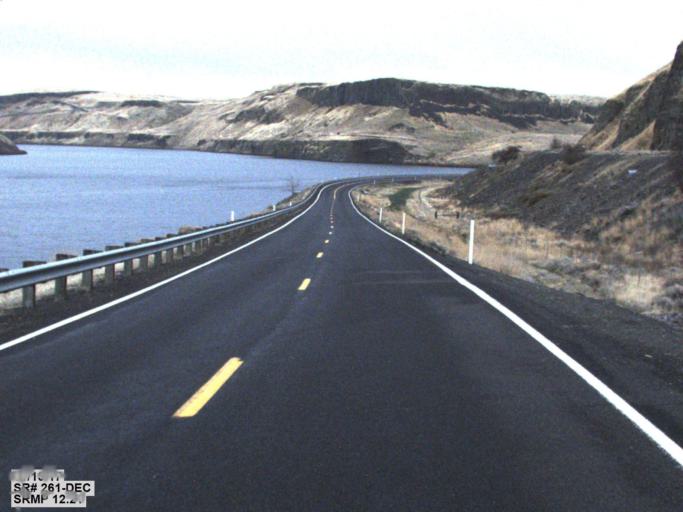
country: US
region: Washington
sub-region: Walla Walla County
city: Waitsburg
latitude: 46.5604
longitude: -118.1827
